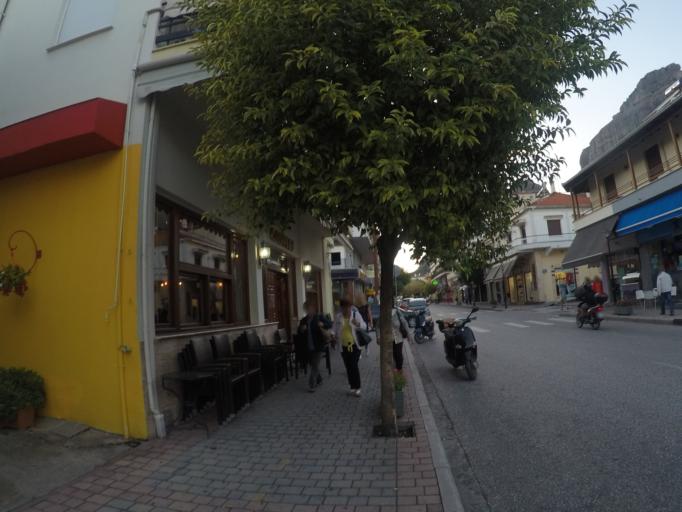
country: GR
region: Thessaly
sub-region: Trikala
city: Kalampaka
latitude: 39.7047
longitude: 21.6275
